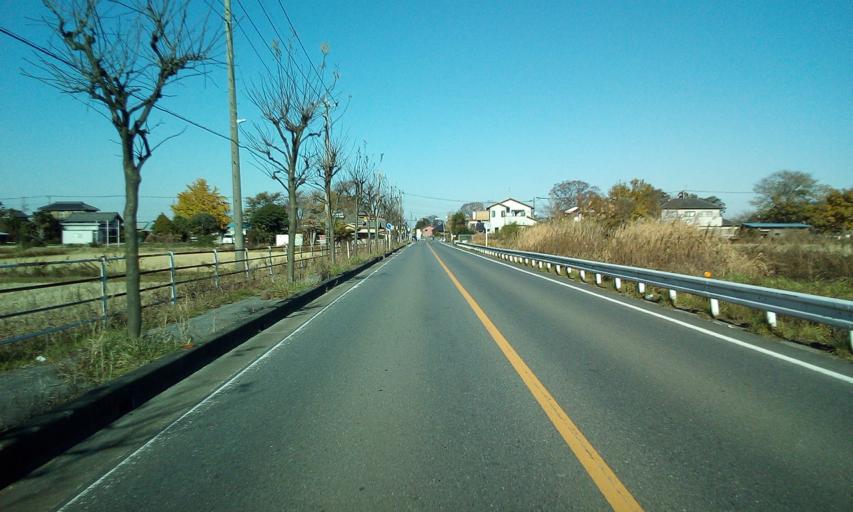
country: JP
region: Saitama
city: Kasukabe
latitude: 36.0017
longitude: 139.7956
